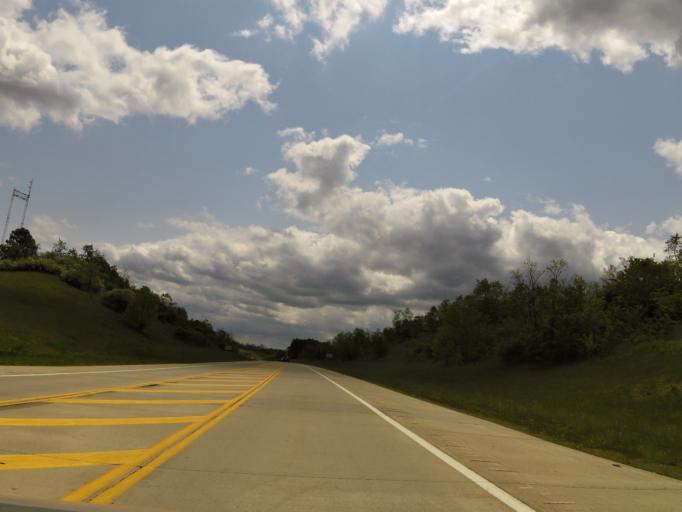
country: US
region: Ohio
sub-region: Athens County
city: Athens
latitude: 39.2375
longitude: -82.0740
